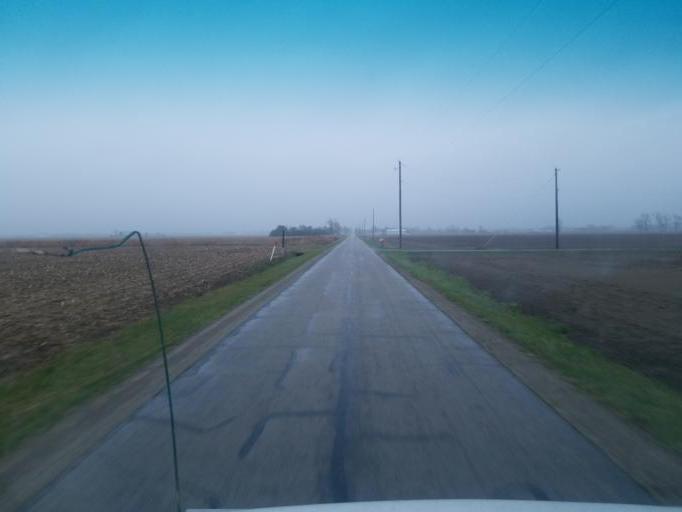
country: US
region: Ohio
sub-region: Henry County
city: Napoleon
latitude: 41.4133
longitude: -84.2221
